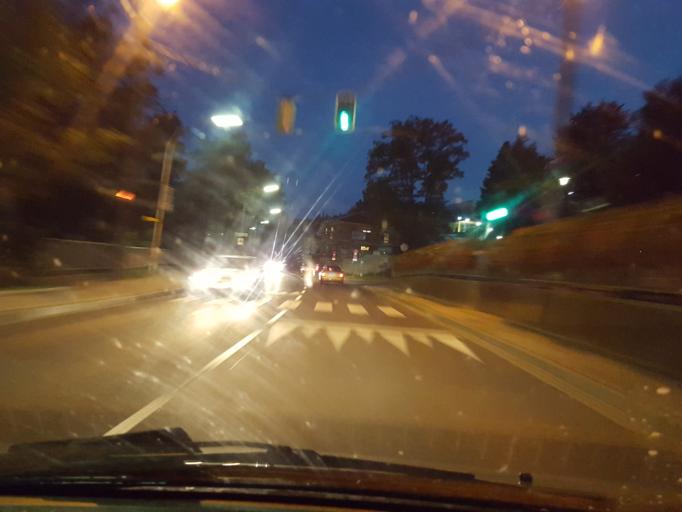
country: AT
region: Lower Austria
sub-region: Politischer Bezirk Scheibbs
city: Wieselburg
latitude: 48.1268
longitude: 15.1379
